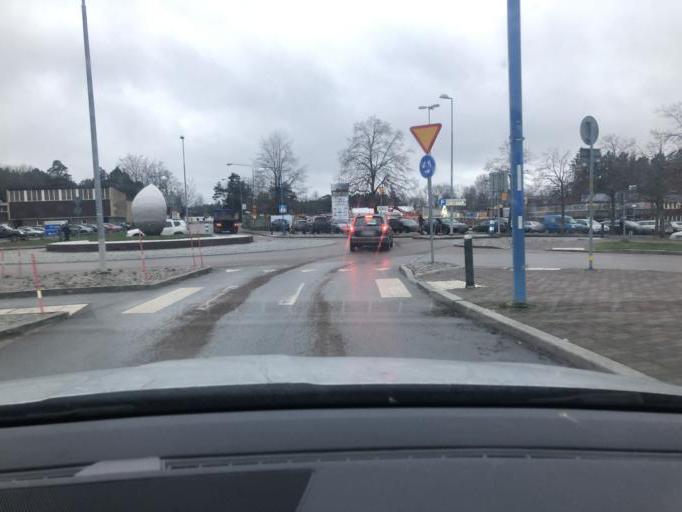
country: SE
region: Vaermland
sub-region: Karlstads Kommun
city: Karlstad
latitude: 59.3741
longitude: 13.4814
